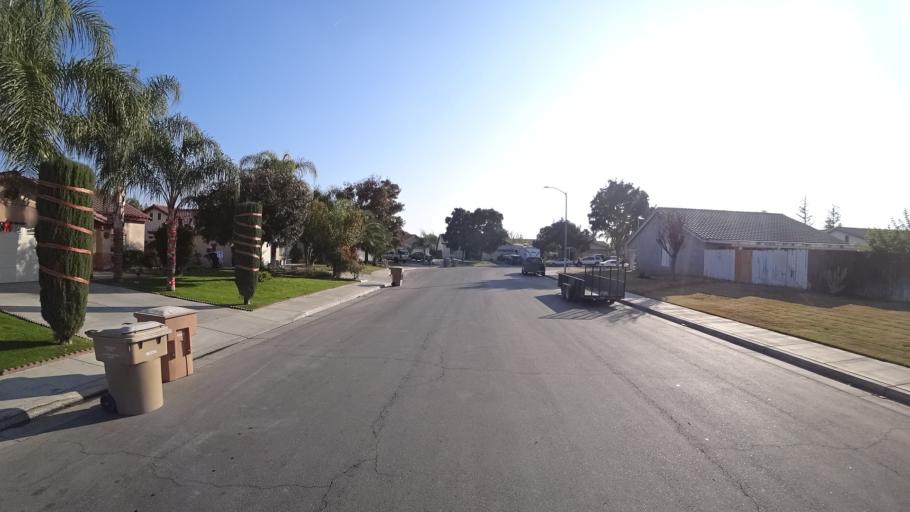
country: US
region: California
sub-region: Kern County
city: Greenfield
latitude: 35.2899
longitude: -119.0129
